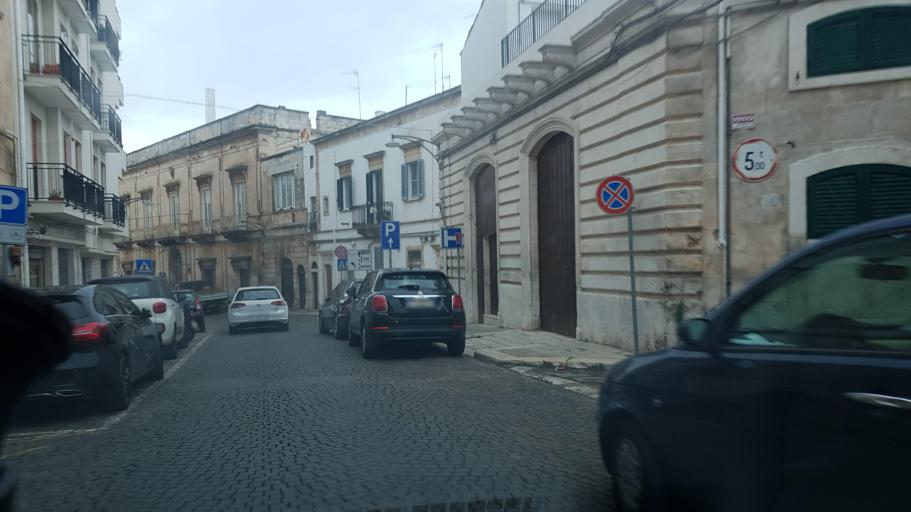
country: IT
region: Apulia
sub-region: Provincia di Brindisi
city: Ostuni
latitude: 40.7305
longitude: 17.5812
